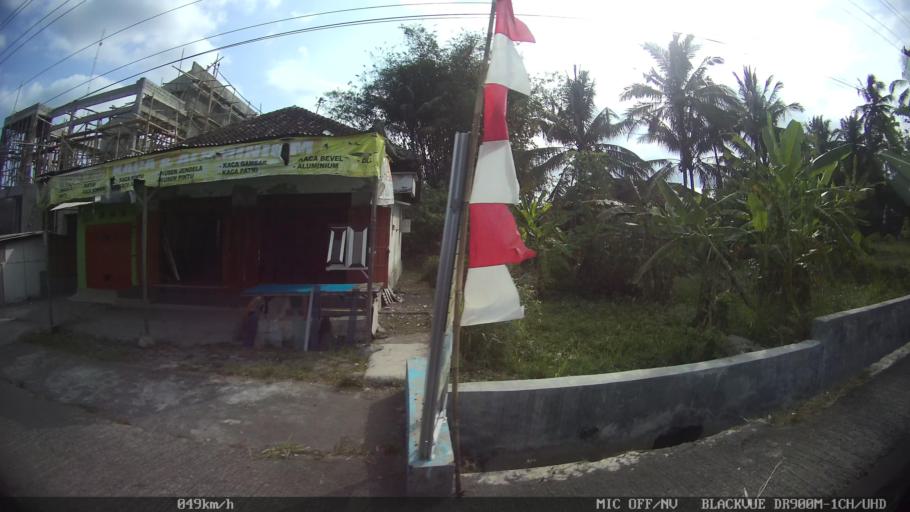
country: ID
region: Central Java
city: Candi Prambanan
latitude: -7.6909
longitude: 110.4622
